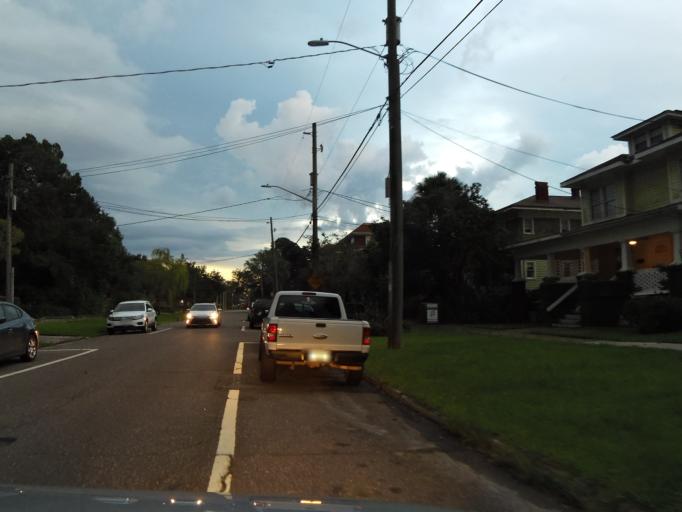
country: US
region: Florida
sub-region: Duval County
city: Jacksonville
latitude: 30.3084
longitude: -81.6936
